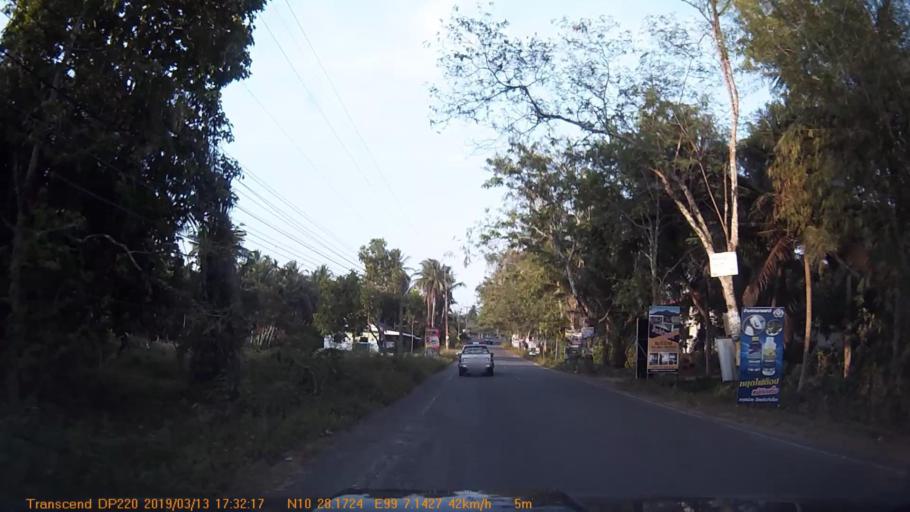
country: TH
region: Chumphon
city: Chumphon
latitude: 10.4698
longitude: 99.1192
